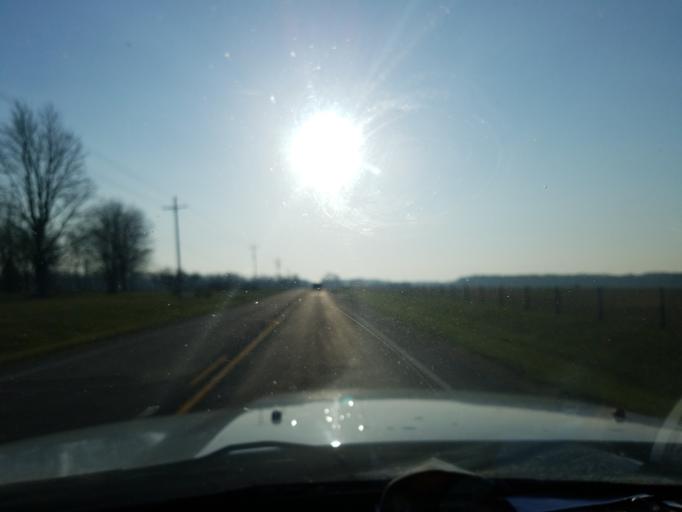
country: US
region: Indiana
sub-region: Vigo County
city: Seelyville
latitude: 39.3902
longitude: -87.2893
